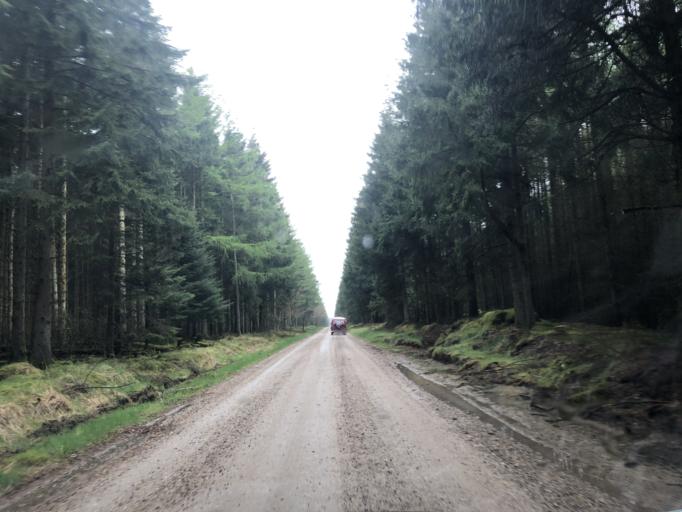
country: DK
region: Central Jutland
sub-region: Lemvig Kommune
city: Lemvig
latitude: 56.4666
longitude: 8.3922
